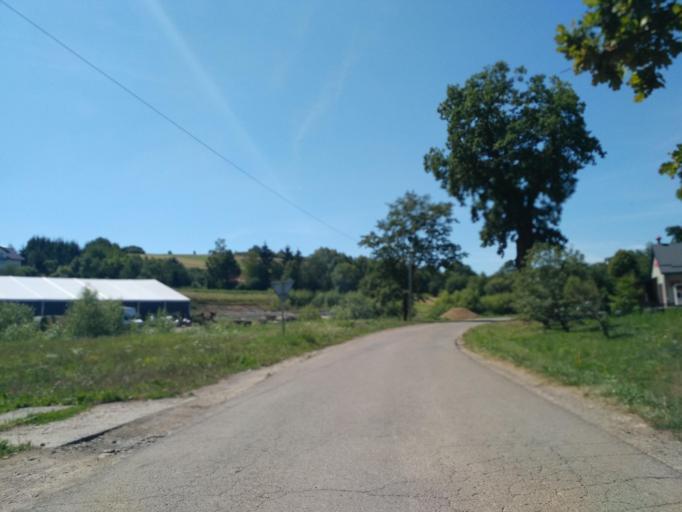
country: PL
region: Subcarpathian Voivodeship
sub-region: Powiat sanocki
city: Nowosielce-Gniewosz
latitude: 49.5395
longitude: 22.0570
